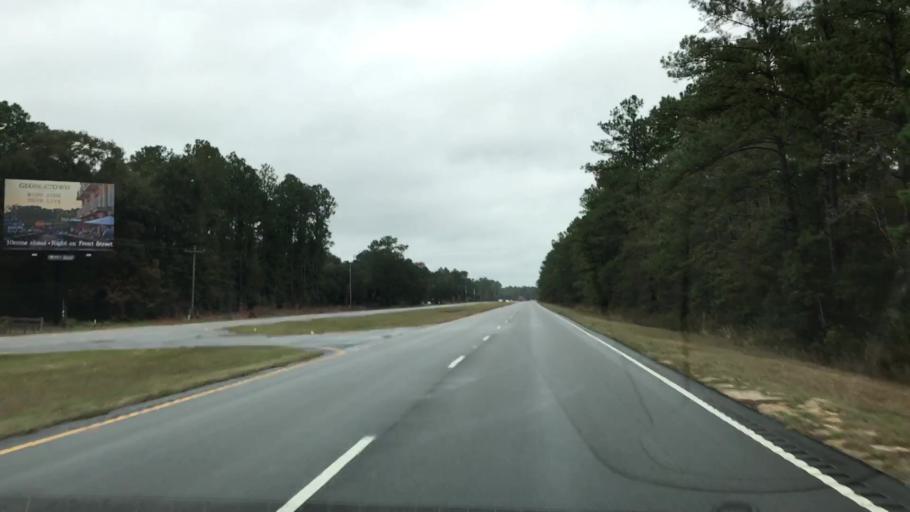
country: US
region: South Carolina
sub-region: Georgetown County
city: Georgetown
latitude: 33.2377
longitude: -79.3757
